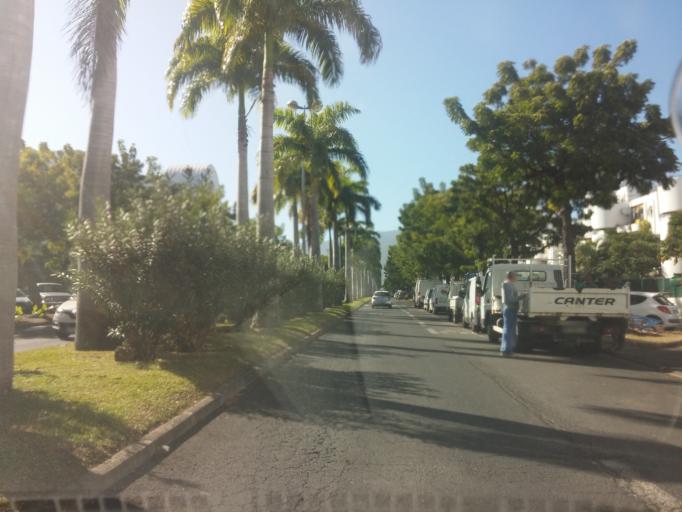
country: RE
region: Reunion
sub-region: Reunion
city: Le Port
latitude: -20.9393
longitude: 55.3009
